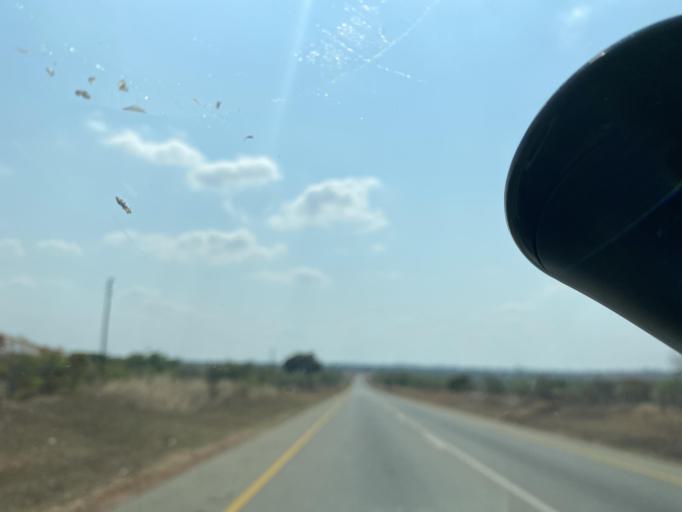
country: ZM
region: Lusaka
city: Chongwe
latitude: -15.5299
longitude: 28.6238
